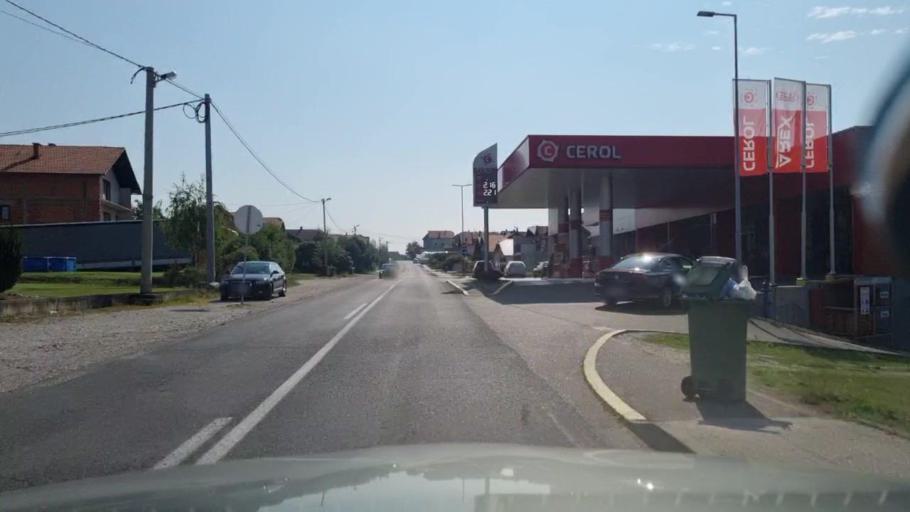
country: BA
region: Federation of Bosnia and Herzegovina
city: Mionica
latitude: 44.8669
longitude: 18.4717
